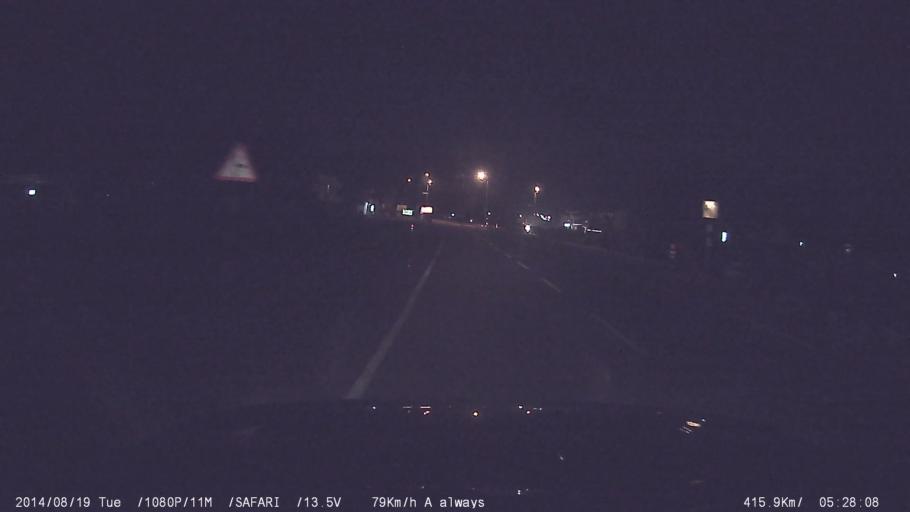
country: IN
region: Tamil Nadu
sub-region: Salem
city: Attayyampatti
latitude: 11.5918
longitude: 78.0751
